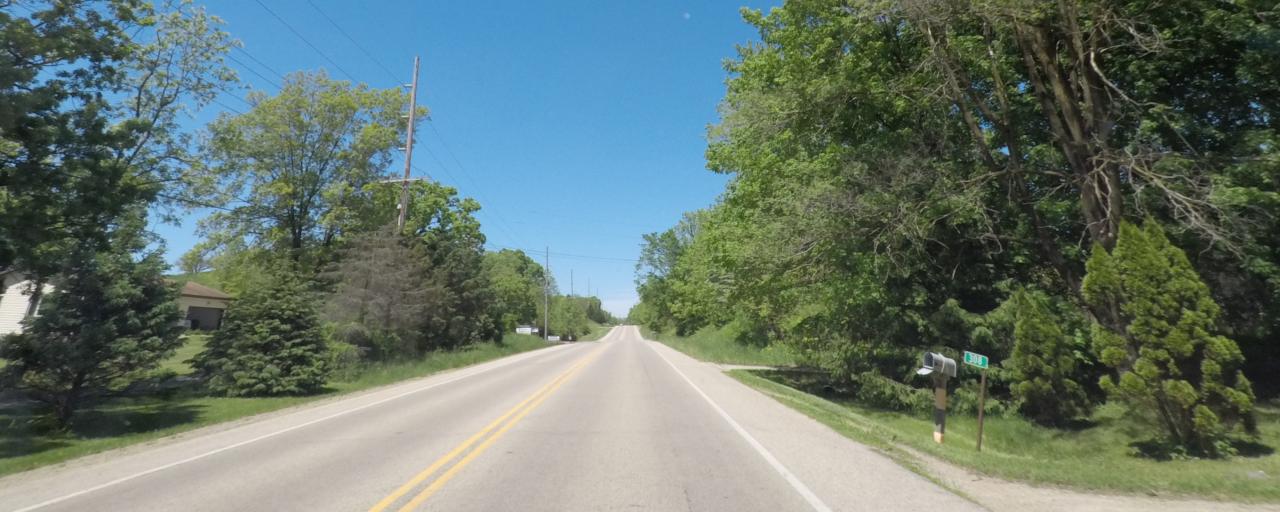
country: US
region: Wisconsin
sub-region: Green County
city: Brooklyn
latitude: 42.8702
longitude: -89.3691
